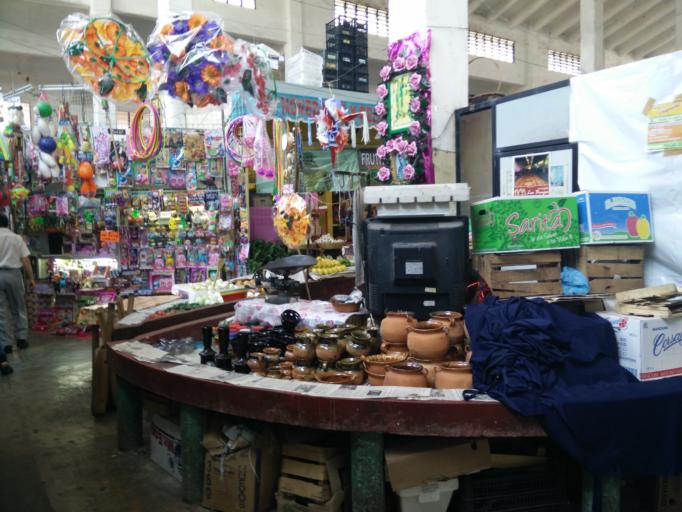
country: MX
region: Veracruz
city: Coatepec
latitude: 19.4546
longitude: -96.9618
